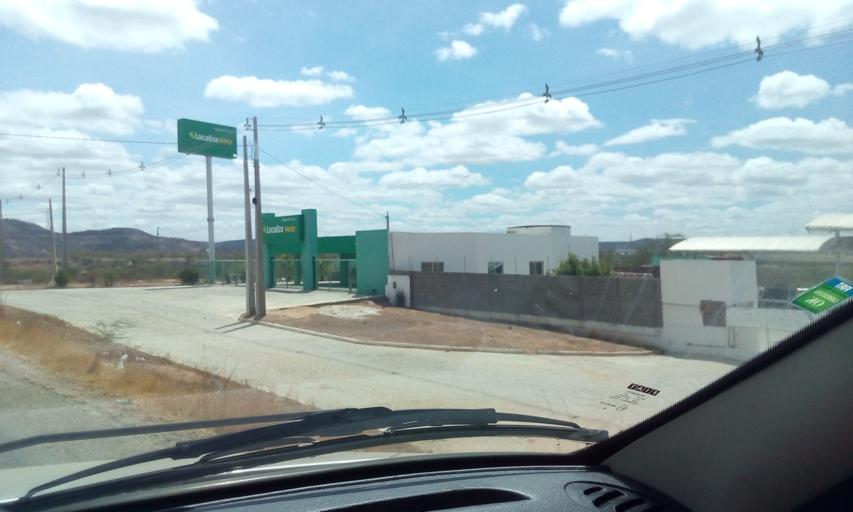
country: BR
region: Rio Grande do Norte
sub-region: Currais Novos
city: Currais Novos
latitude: -6.2777
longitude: -36.5242
